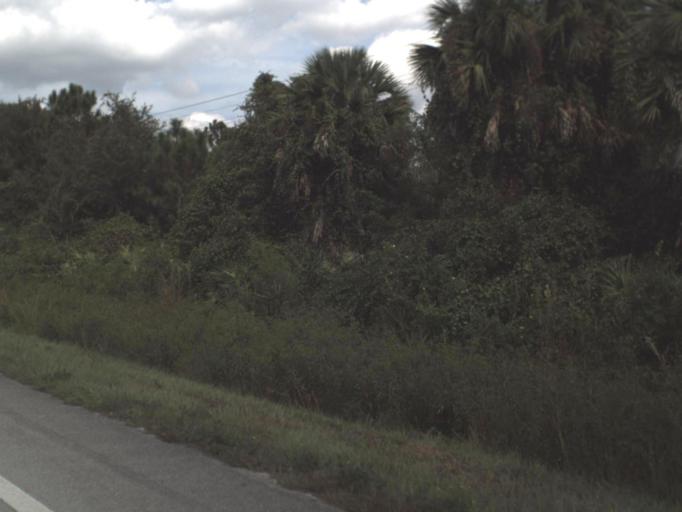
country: US
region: Florida
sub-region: Okeechobee County
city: Cypress Quarters
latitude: 27.3494
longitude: -80.8216
